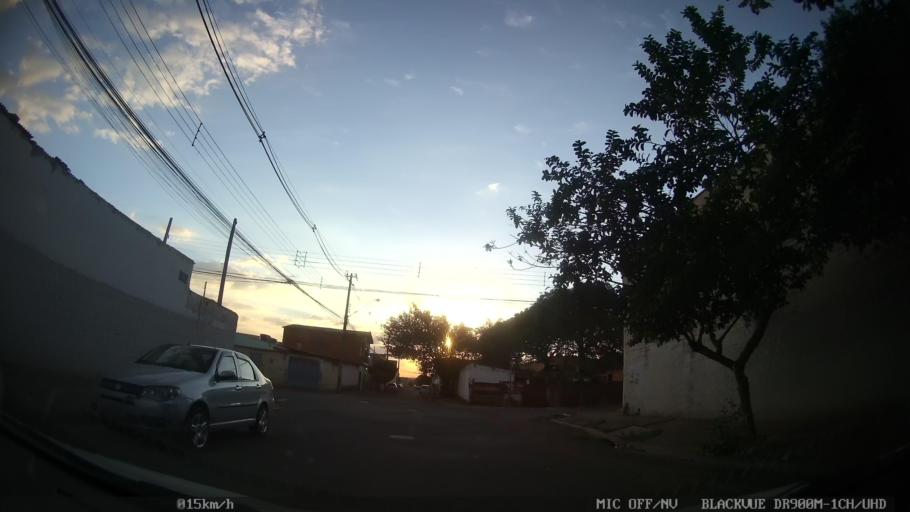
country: BR
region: Sao Paulo
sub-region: Ribeirao Preto
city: Ribeirao Preto
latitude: -21.1452
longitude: -47.7910
